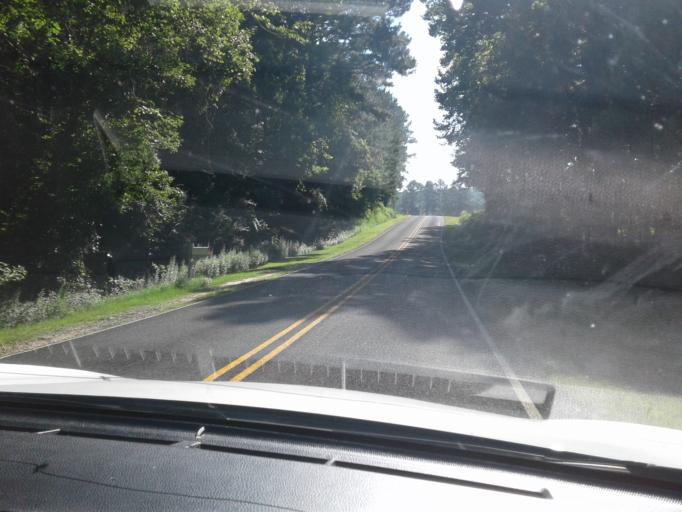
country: US
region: North Carolina
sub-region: Harnett County
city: Lillington
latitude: 35.4663
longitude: -78.8643
